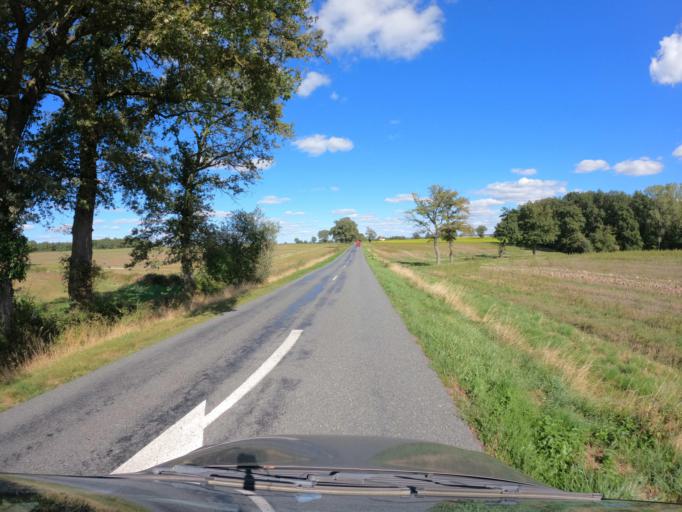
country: FR
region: Auvergne
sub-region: Departement de l'Allier
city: Doyet
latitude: 46.3864
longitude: 2.7949
